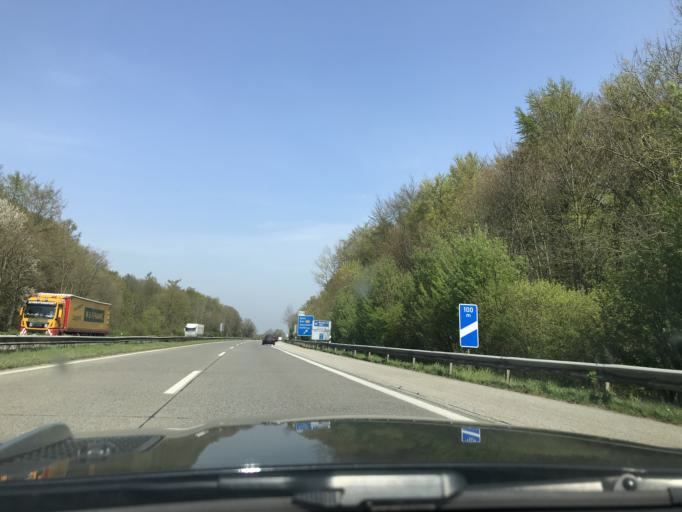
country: DE
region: Schleswig-Holstein
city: Susel
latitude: 54.0505
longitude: 10.7323
